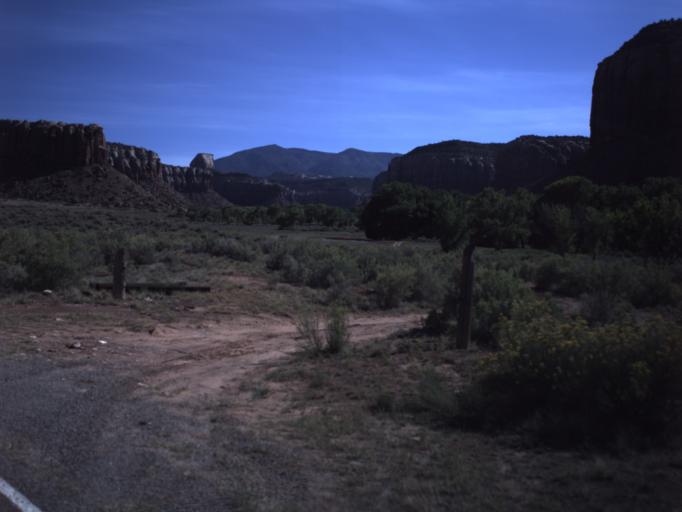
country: US
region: Utah
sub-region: San Juan County
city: Monticello
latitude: 38.0691
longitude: -109.5561
